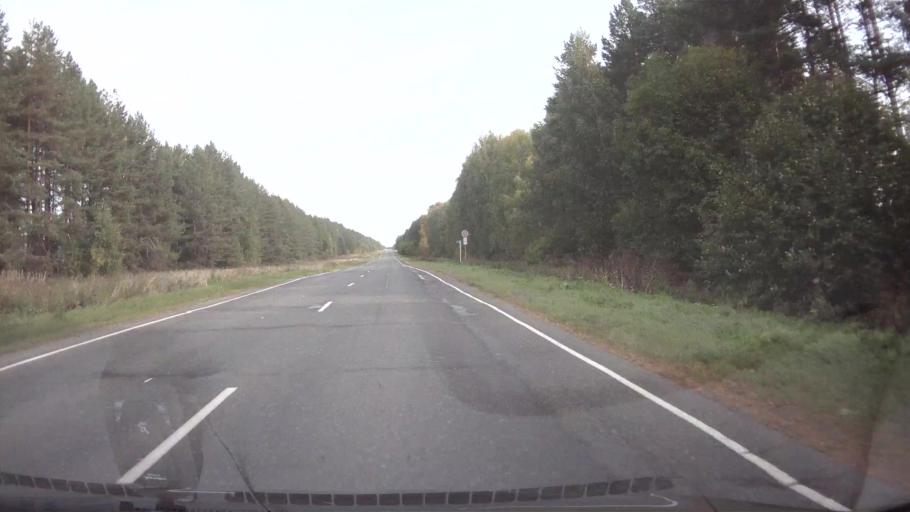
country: RU
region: Mariy-El
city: Kuzhener
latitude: 56.8231
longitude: 48.7202
